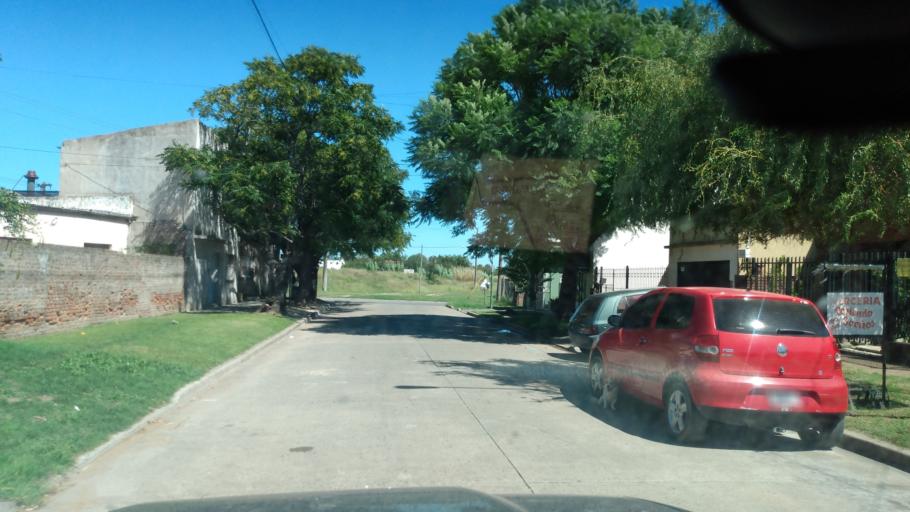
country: AR
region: Buenos Aires
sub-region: Partido de Lujan
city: Lujan
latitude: -34.5798
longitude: -59.1128
